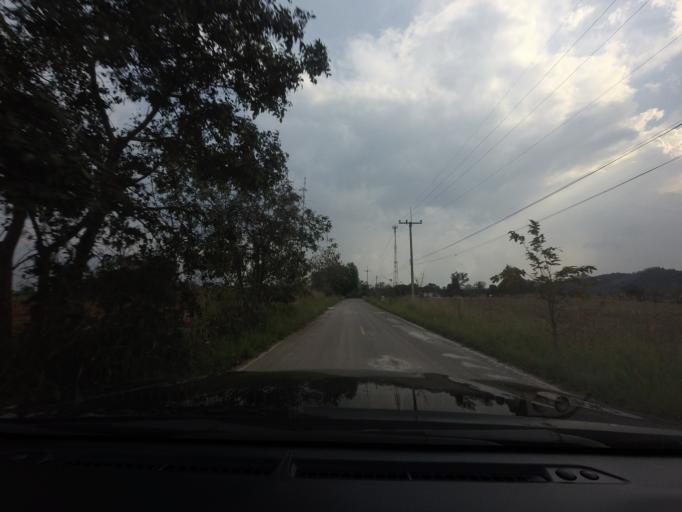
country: TH
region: Nakhon Ratchasima
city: Wang Nam Khiao
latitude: 14.3968
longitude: 101.7945
